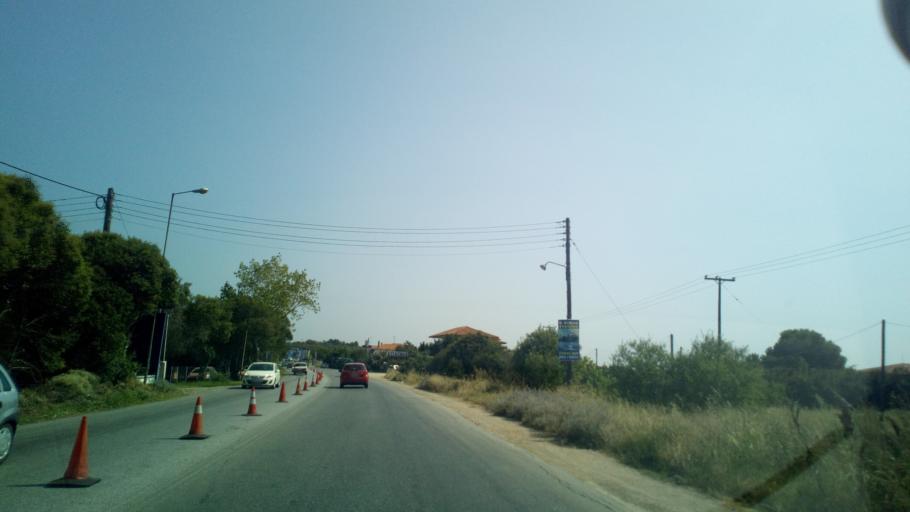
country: GR
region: Central Macedonia
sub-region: Nomos Chalkidikis
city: Nea Potidhaia
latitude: 40.2053
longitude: 23.3238
